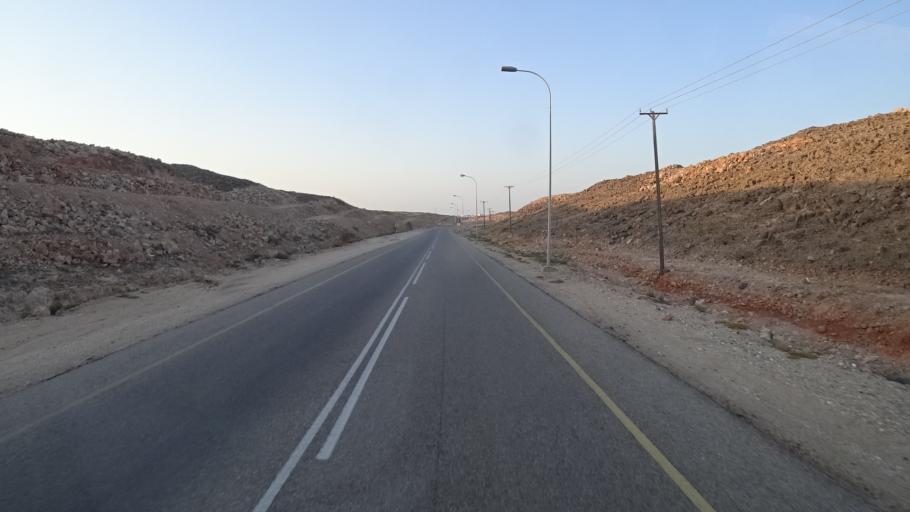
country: OM
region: Ash Sharqiyah
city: Sur
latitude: 22.4995
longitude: 59.7914
